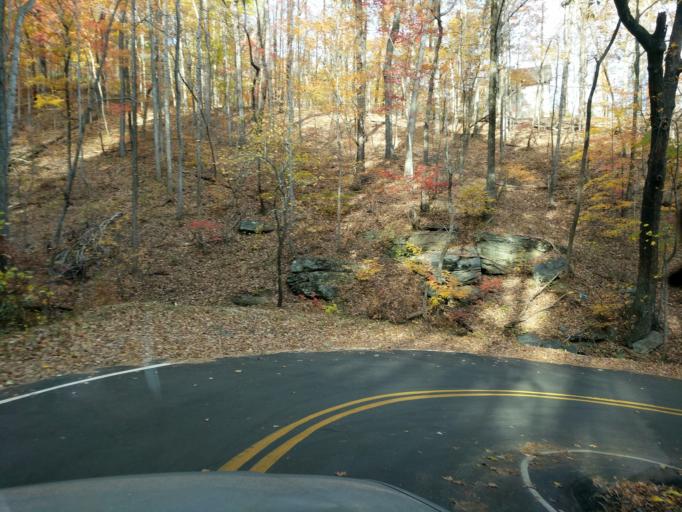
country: US
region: North Carolina
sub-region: Polk County
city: Columbus
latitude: 35.2613
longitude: -82.2324
